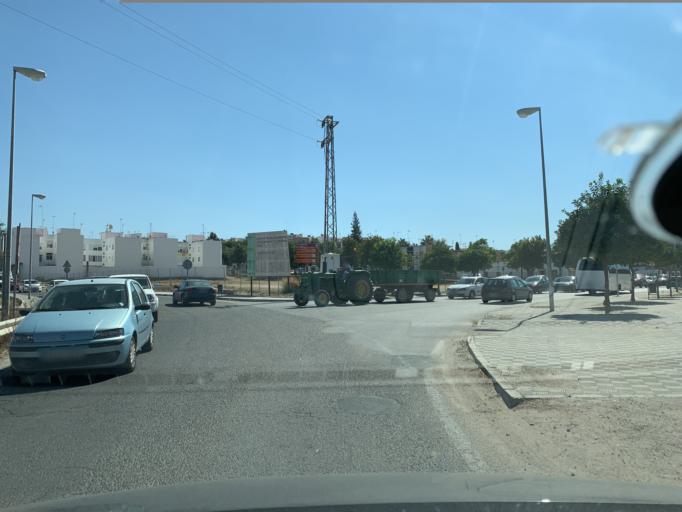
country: ES
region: Andalusia
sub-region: Provincia de Sevilla
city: Marchena
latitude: 37.3348
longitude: -5.4232
